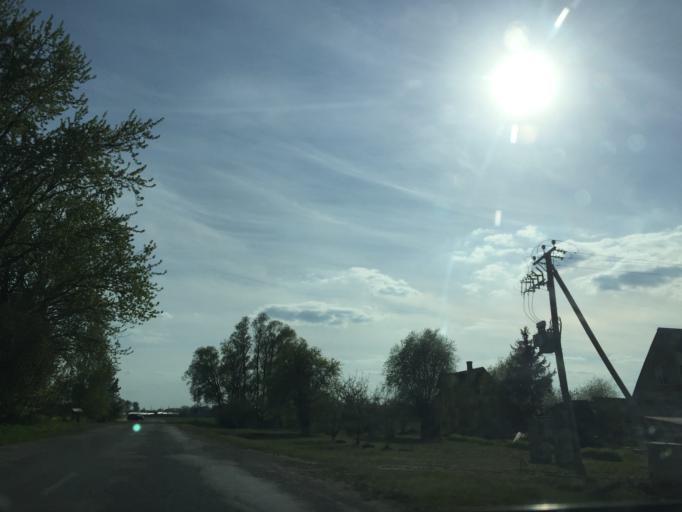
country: LV
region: Bauskas Rajons
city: Bauska
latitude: 56.4484
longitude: 24.2527
